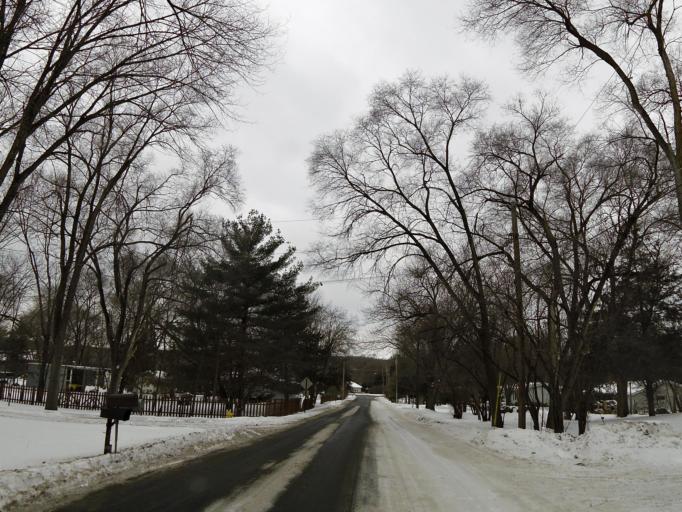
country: US
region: Minnesota
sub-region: Washington County
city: Lakeland
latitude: 44.9517
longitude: -92.7685
